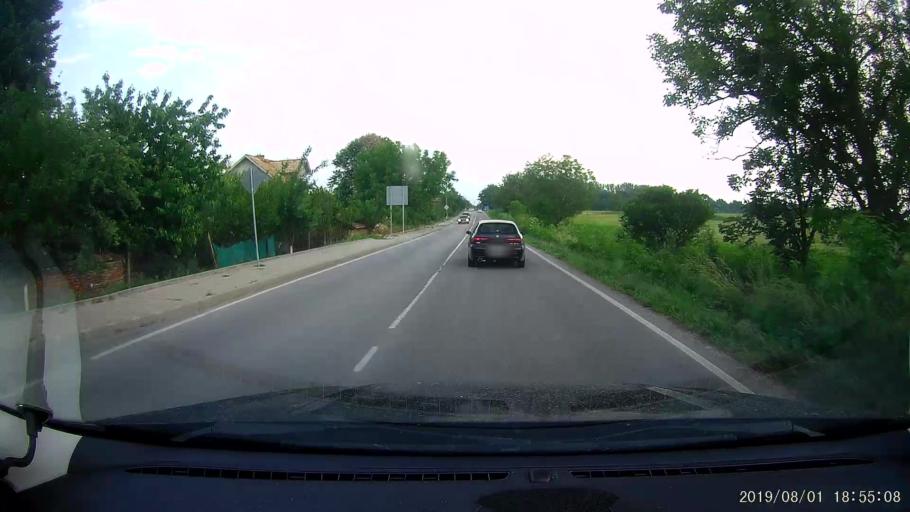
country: BG
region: Shumen
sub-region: Obshtina Shumen
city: Shumen
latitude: 43.1854
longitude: 27.0042
